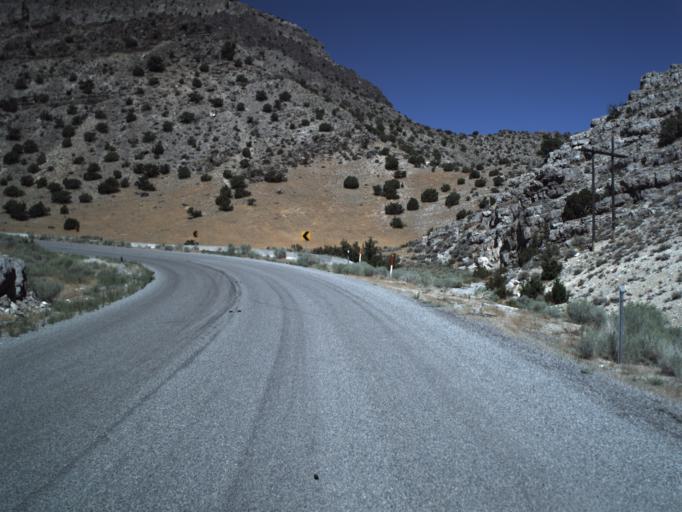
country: US
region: Utah
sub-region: Beaver County
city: Milford
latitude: 39.0855
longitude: -113.5772
